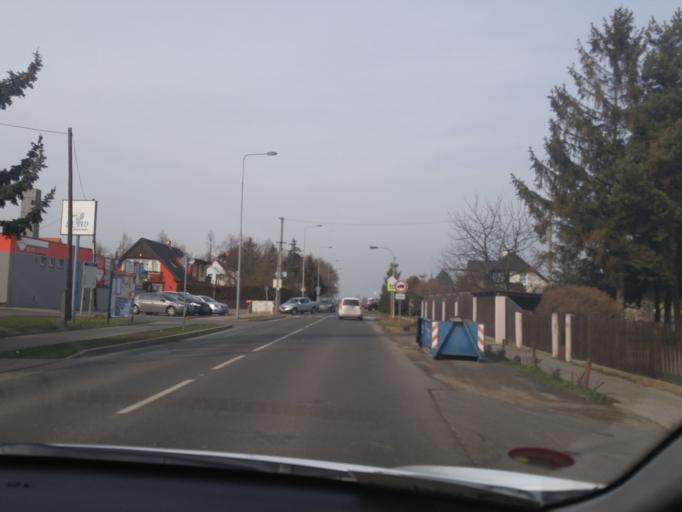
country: CZ
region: Central Bohemia
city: Brandys nad Labem-Stara Boleslav
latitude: 50.1897
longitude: 14.6505
